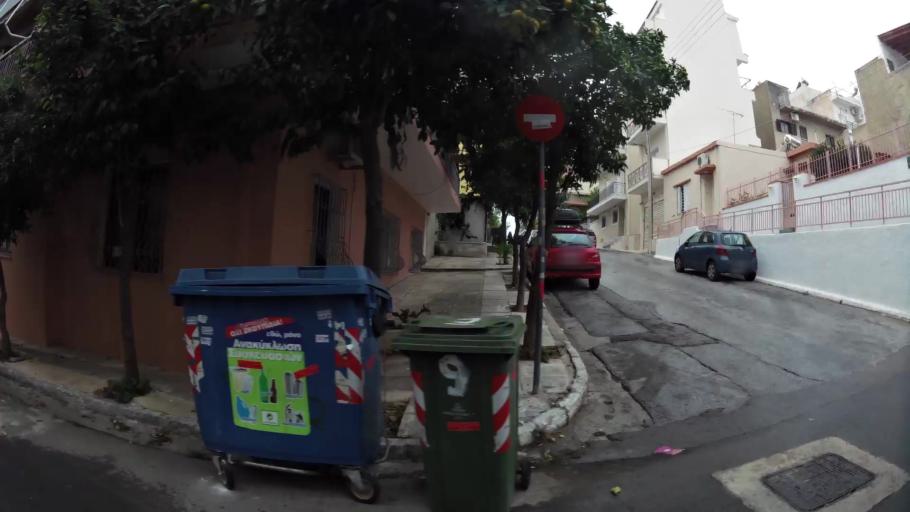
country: GR
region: Attica
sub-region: Nomarchia Athinas
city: Agia Varvara
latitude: 37.9873
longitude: 23.6544
